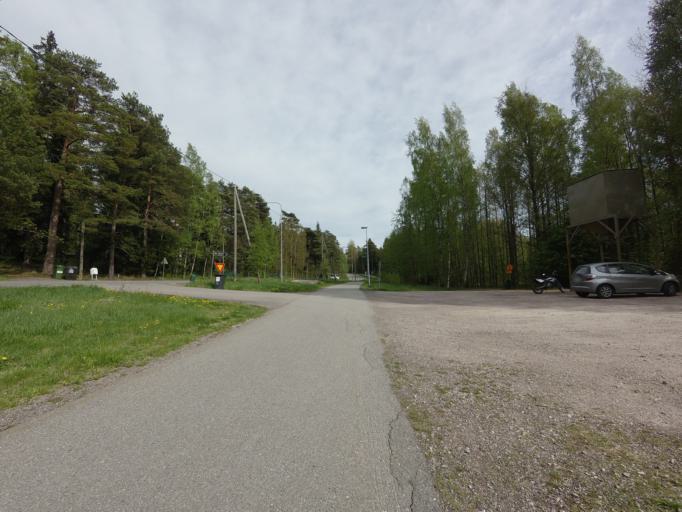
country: FI
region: Uusimaa
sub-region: Helsinki
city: Koukkuniemi
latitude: 60.1269
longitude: 24.7095
